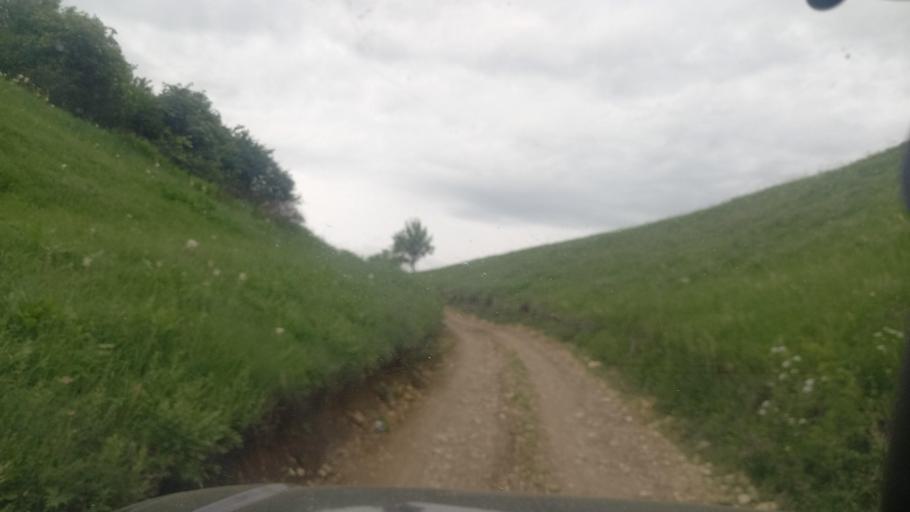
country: RU
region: Krasnodarskiy
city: Peredovaya
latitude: 44.0809
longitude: 41.3653
